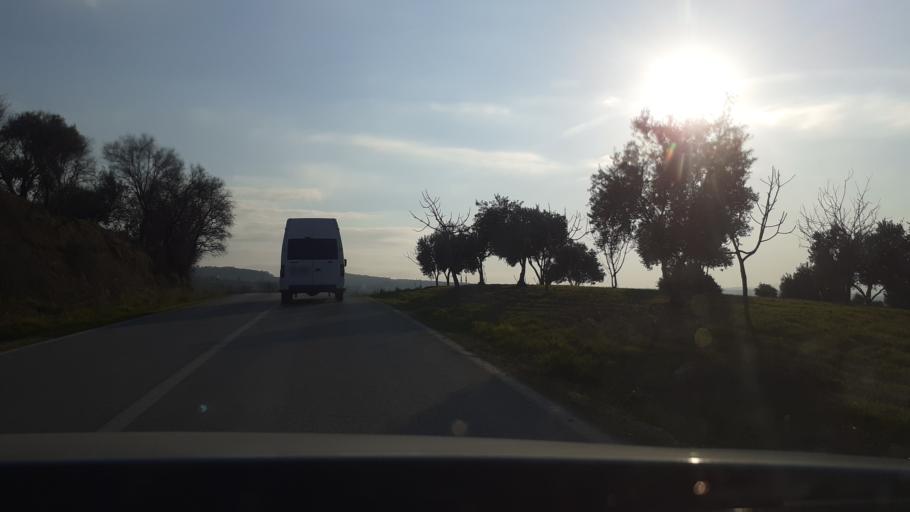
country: TR
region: Hatay
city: Oymakli
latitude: 36.1208
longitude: 36.3056
